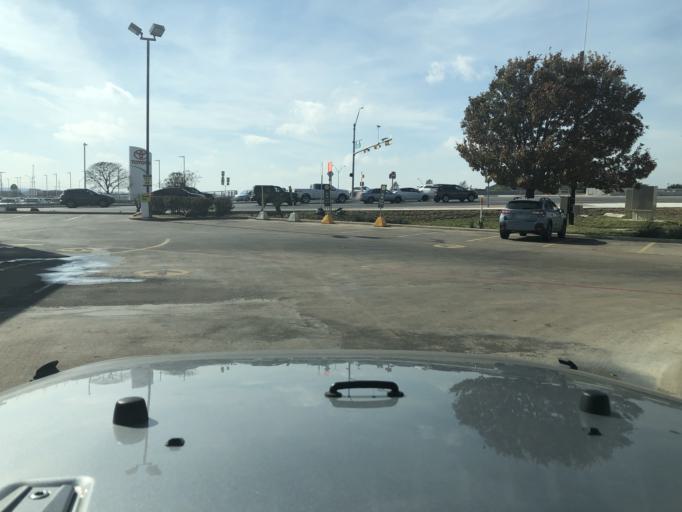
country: US
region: Texas
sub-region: Williamson County
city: Round Rock
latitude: 30.5354
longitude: -97.6908
